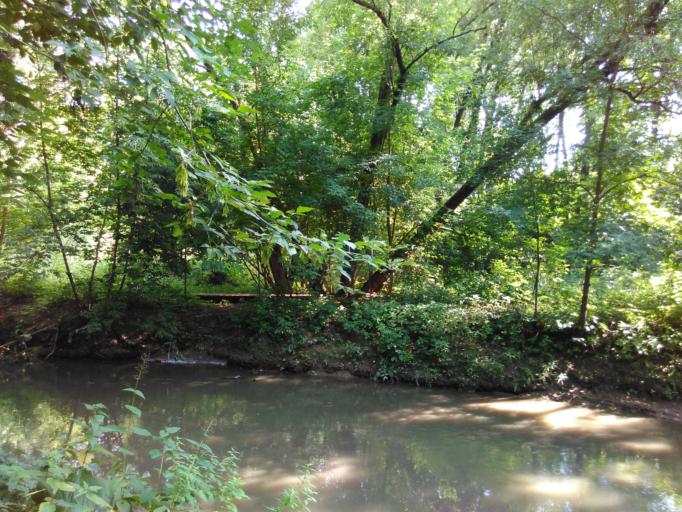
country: RU
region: Moskovskaya
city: Bol'shaya Setun'
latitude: 55.7161
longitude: 37.4255
